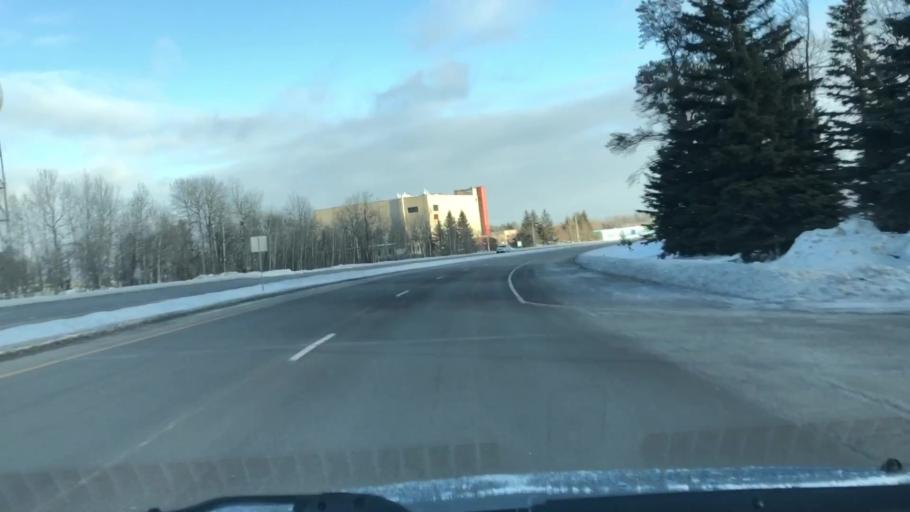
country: US
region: Minnesota
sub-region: Saint Louis County
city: Hermantown
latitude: 46.8365
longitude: -92.2116
